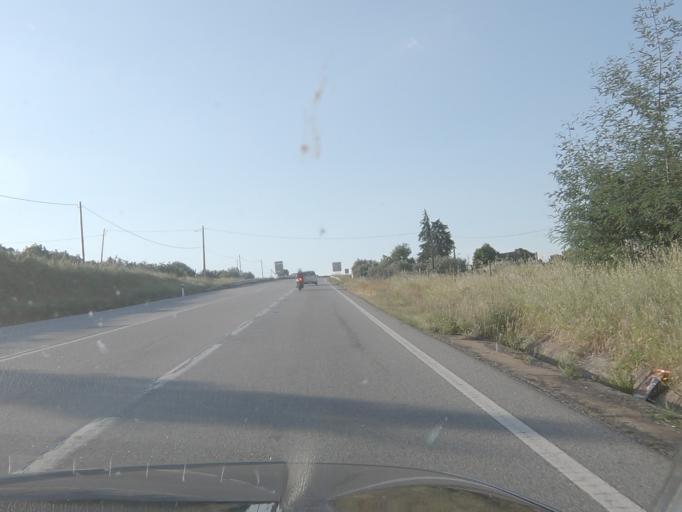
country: PT
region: Portalegre
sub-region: Portalegre
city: Portalegre
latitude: 39.3068
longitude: -7.4420
